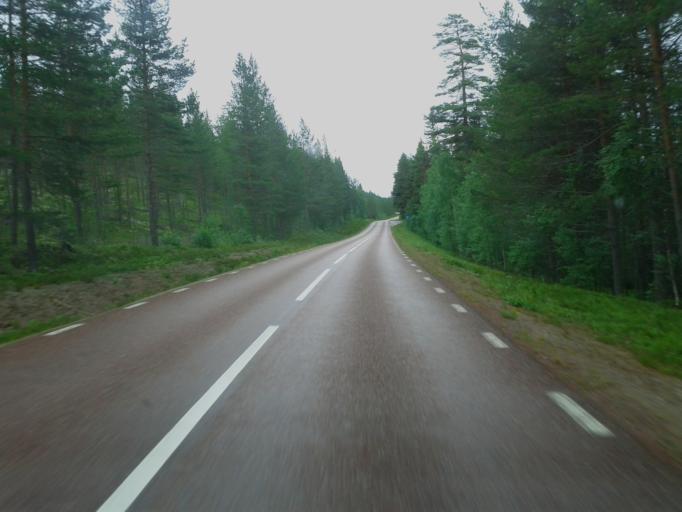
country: NO
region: Hedmark
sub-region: Trysil
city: Innbygda
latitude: 61.7825
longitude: 12.9379
